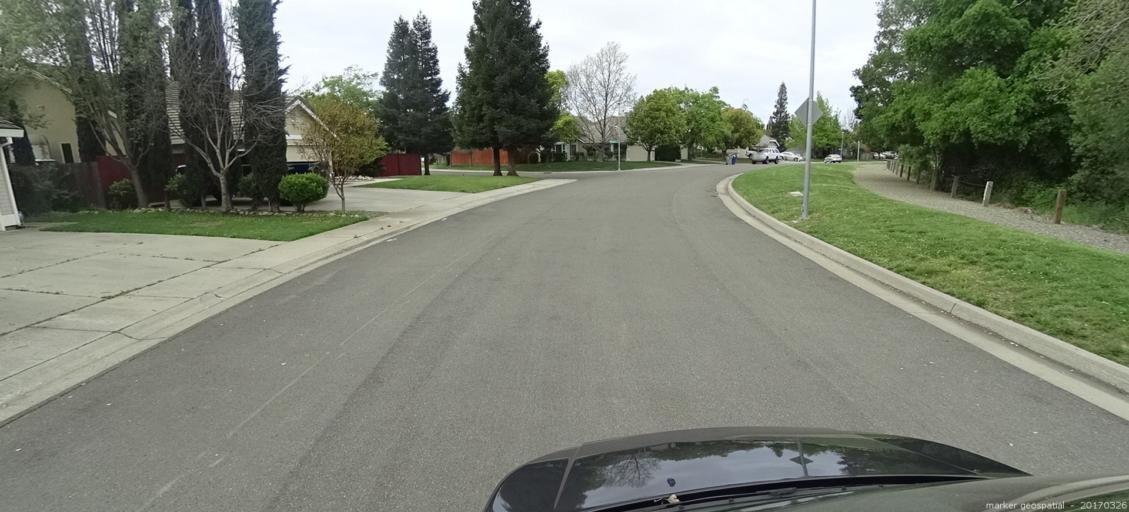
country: US
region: California
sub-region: Sacramento County
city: Laguna
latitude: 38.4429
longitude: -121.4413
